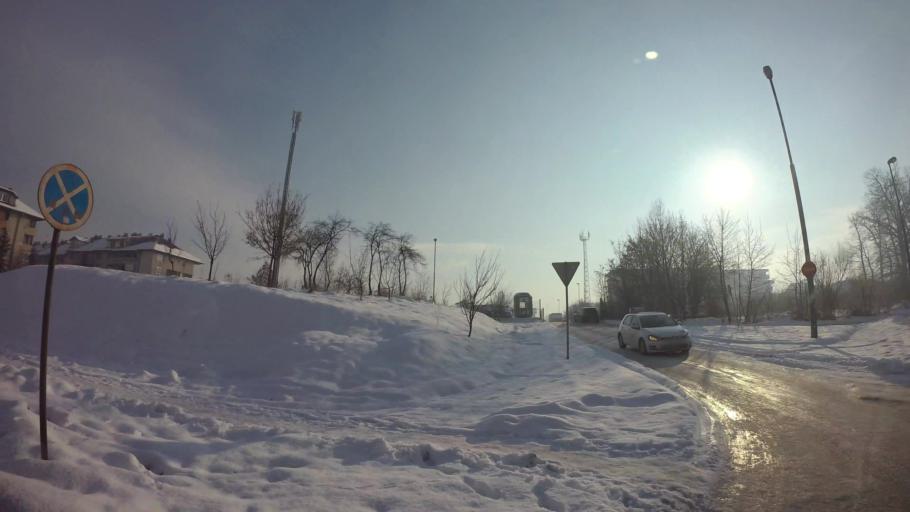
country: BA
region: Federation of Bosnia and Herzegovina
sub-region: Kanton Sarajevo
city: Sarajevo
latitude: 43.8269
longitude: 18.3548
